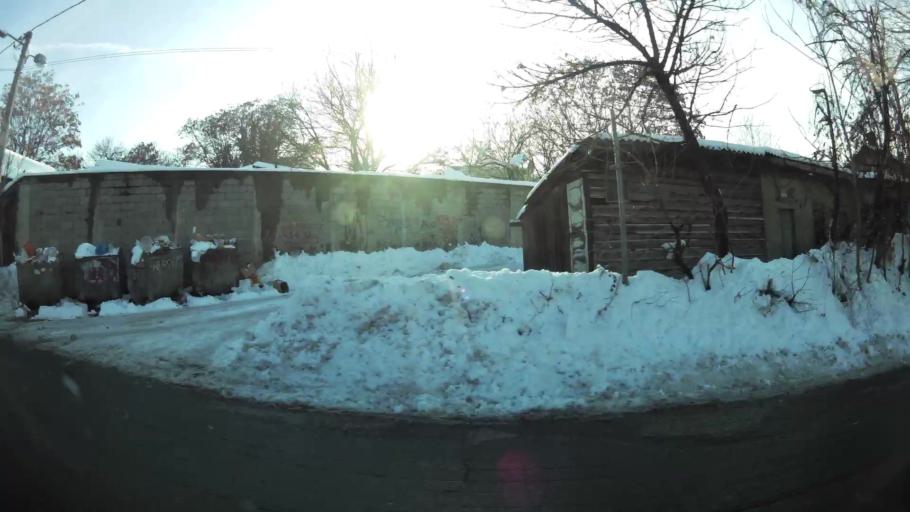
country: RS
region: Central Serbia
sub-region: Belgrade
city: Palilula
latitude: 44.8186
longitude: 20.4952
